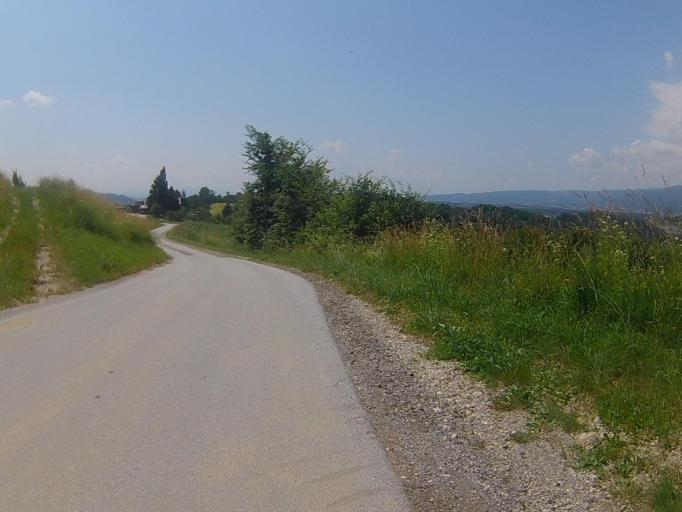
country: SI
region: Pesnica
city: Pesnica pri Mariboru
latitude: 46.5717
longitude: 15.7020
